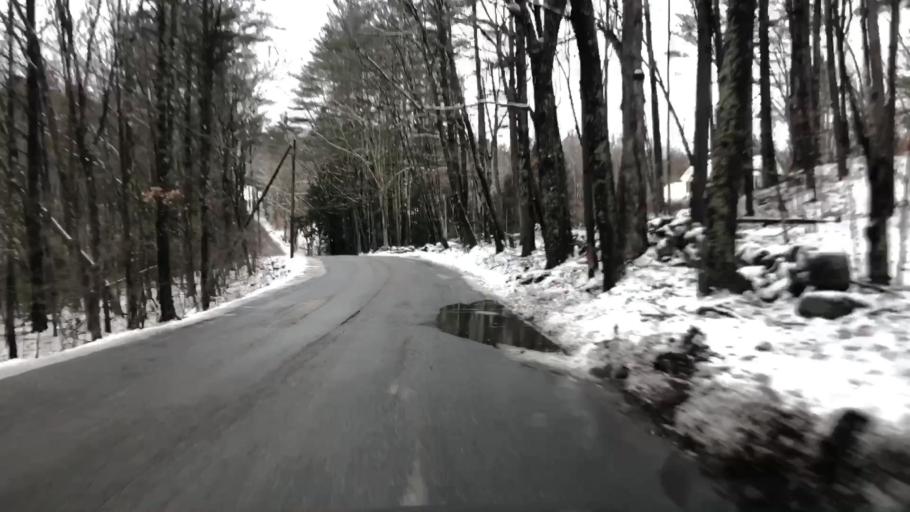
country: US
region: New Hampshire
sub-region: Hillsborough County
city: New Boston
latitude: 43.0105
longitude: -71.6717
